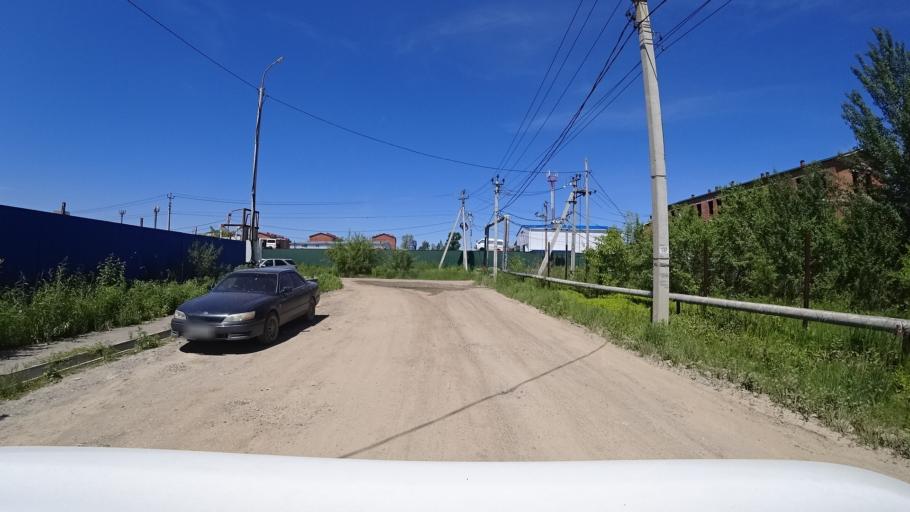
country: RU
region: Khabarovsk Krai
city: Topolevo
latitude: 48.5046
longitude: 135.1811
